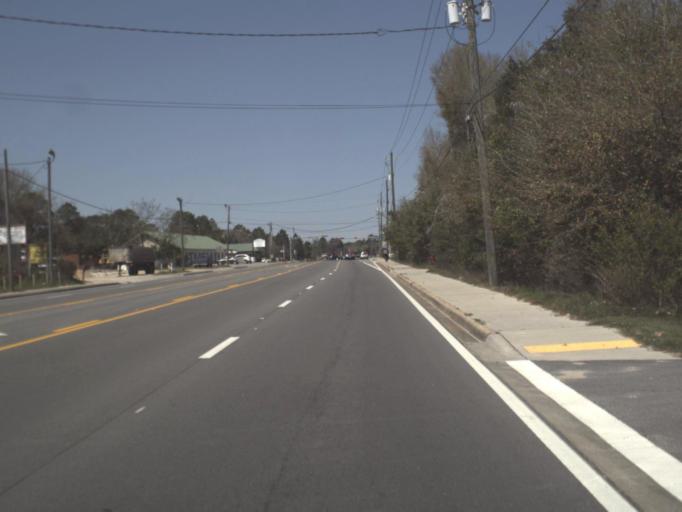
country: US
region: Florida
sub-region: Walton County
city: DeFuniak Springs
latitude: 30.7300
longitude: -86.1375
